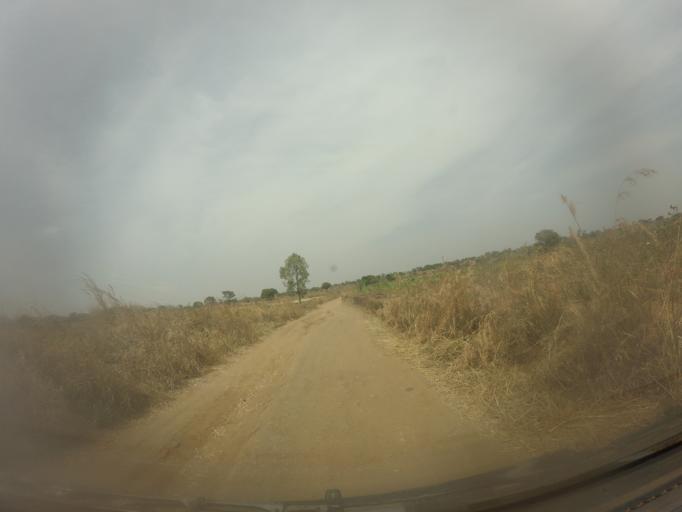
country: UG
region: Northern Region
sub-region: Zombo District
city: Zombo
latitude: 2.7640
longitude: 31.0335
